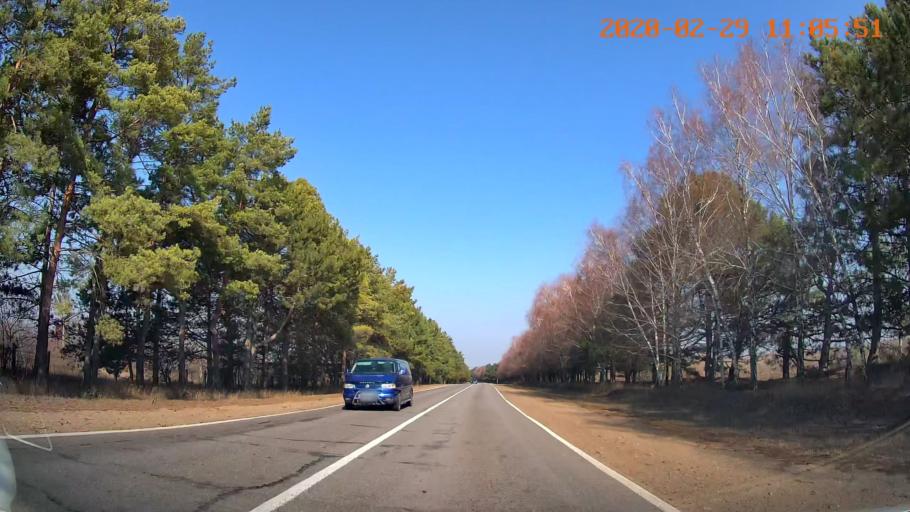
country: MD
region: Criuleni
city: Criuleni
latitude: 47.2072
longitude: 29.1901
